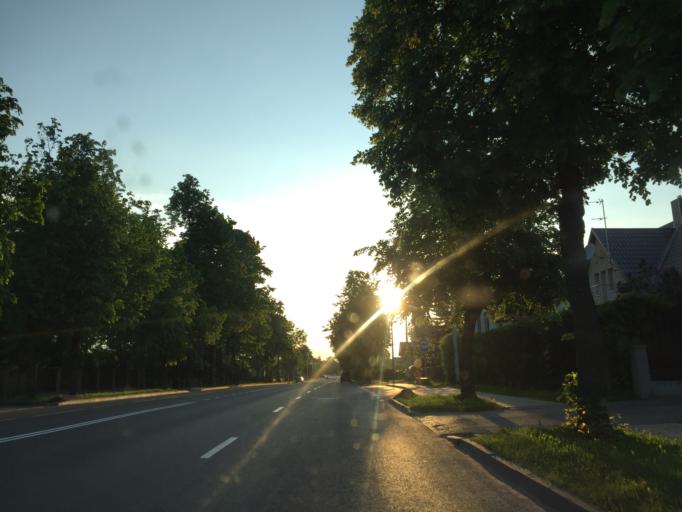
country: LT
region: Siauliu apskritis
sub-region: Siauliai
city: Siauliai
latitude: 55.9413
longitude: 23.2915
